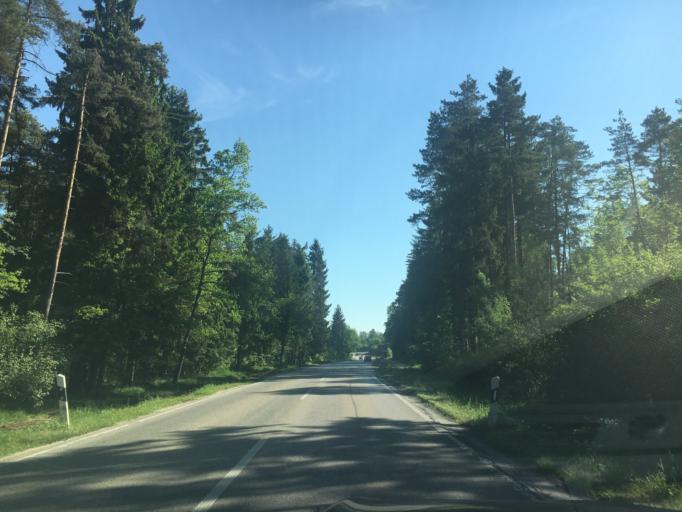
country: DE
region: Bavaria
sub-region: Upper Bavaria
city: Unterneukirchen
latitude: 48.1490
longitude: 12.6091
